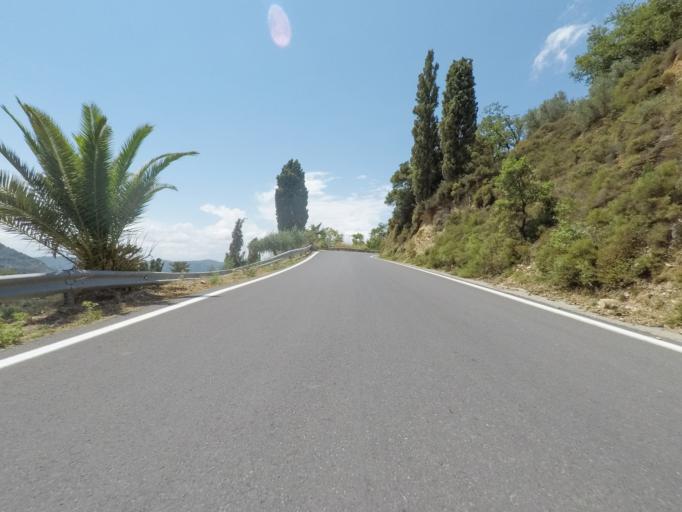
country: GR
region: Crete
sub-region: Nomos Irakleiou
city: Mokhos
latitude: 35.2270
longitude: 25.4617
